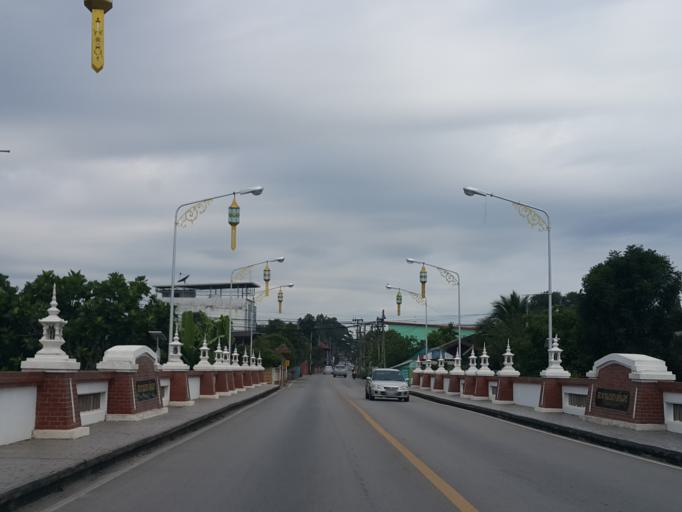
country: TH
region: Lampang
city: Lampang
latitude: 18.2924
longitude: 99.5098
